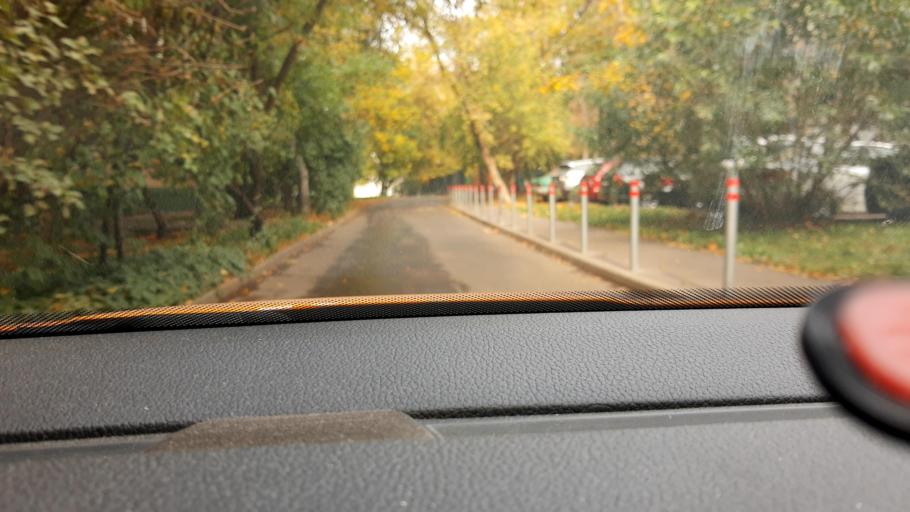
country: RU
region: Moskovskaya
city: Levoberezhnyy
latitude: 55.8456
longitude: 37.4865
